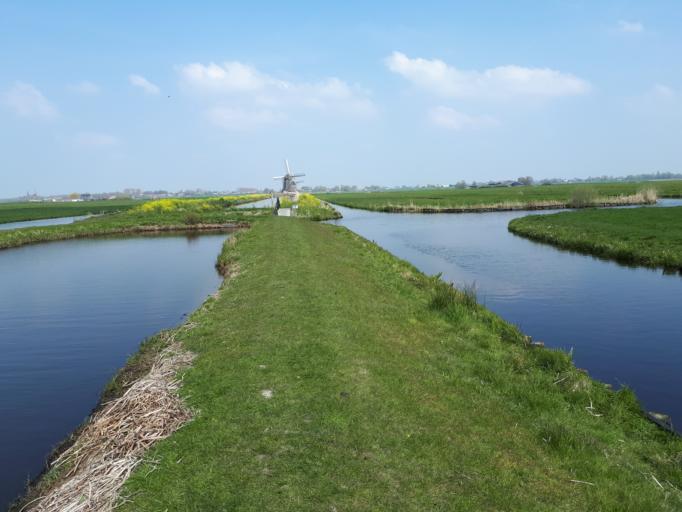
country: NL
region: South Holland
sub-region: Bodegraven-Reeuwijk
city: Bodegraven
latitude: 52.1236
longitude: 4.7189
